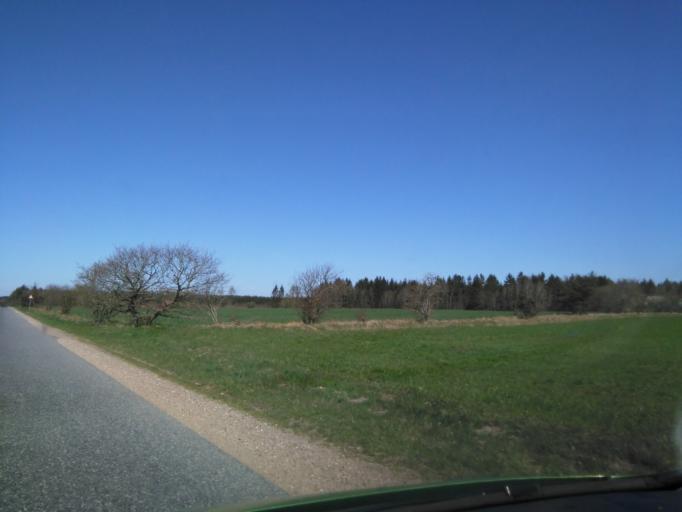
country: DK
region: South Denmark
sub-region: Billund Kommune
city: Billund
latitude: 55.7125
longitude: 9.0917
